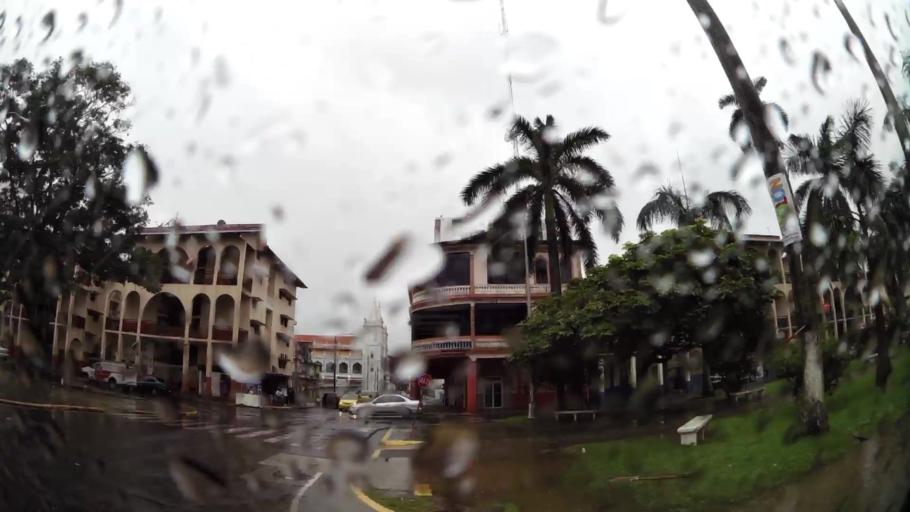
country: PA
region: Colon
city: Colon
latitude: 9.3617
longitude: -79.9027
